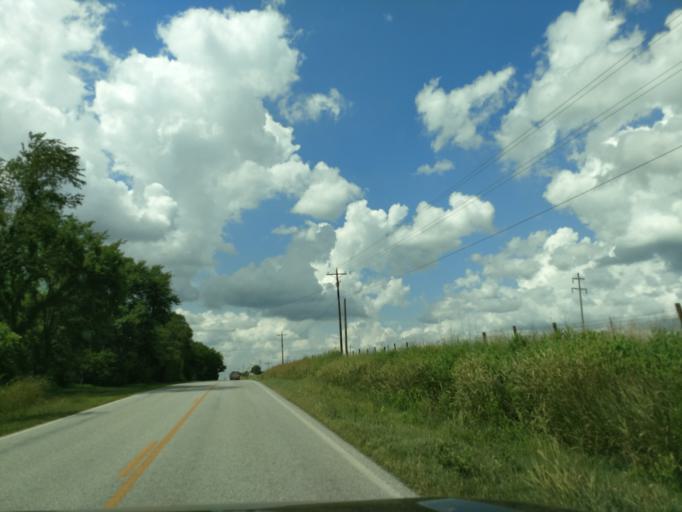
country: US
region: Arkansas
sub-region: Carroll County
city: Berryville
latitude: 36.4641
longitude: -93.5558
